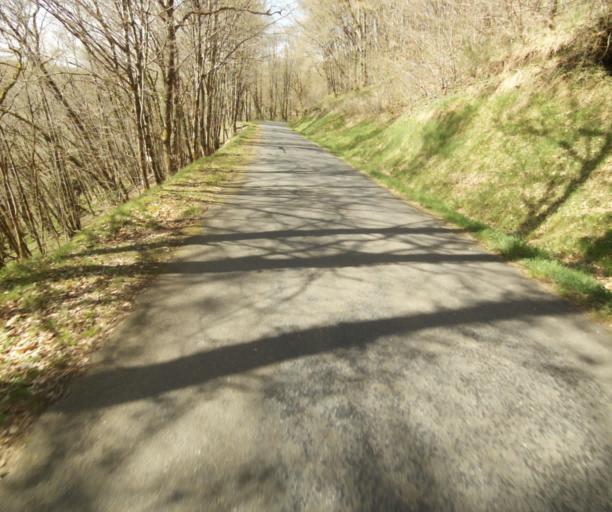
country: FR
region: Limousin
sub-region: Departement de la Correze
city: Naves
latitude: 45.3441
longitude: 1.7817
